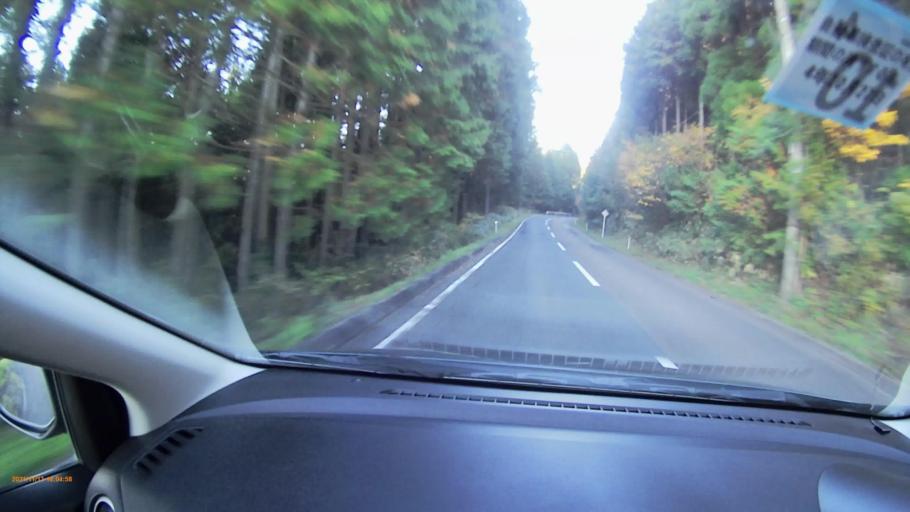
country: JP
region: Gifu
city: Nakatsugawa
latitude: 35.5962
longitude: 137.4701
